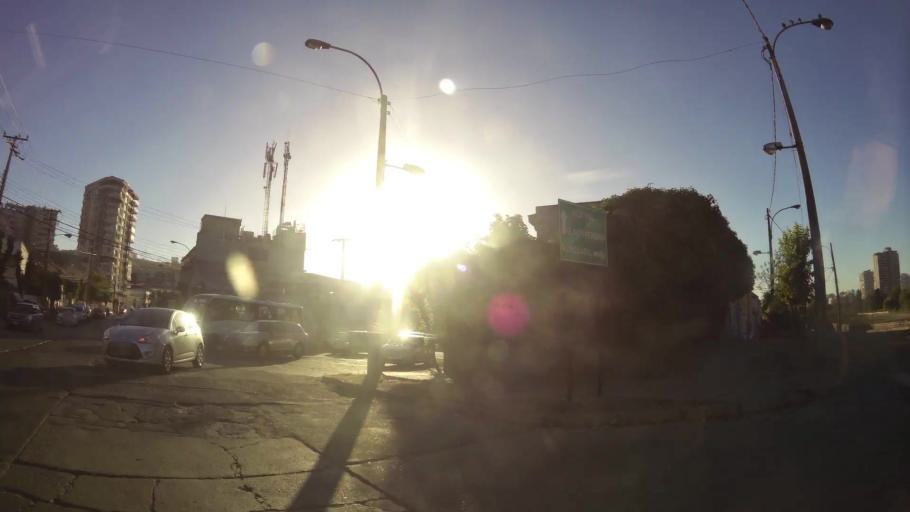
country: CL
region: Valparaiso
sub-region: Provincia de Valparaiso
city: Vina del Mar
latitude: -33.0267
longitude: -71.5395
